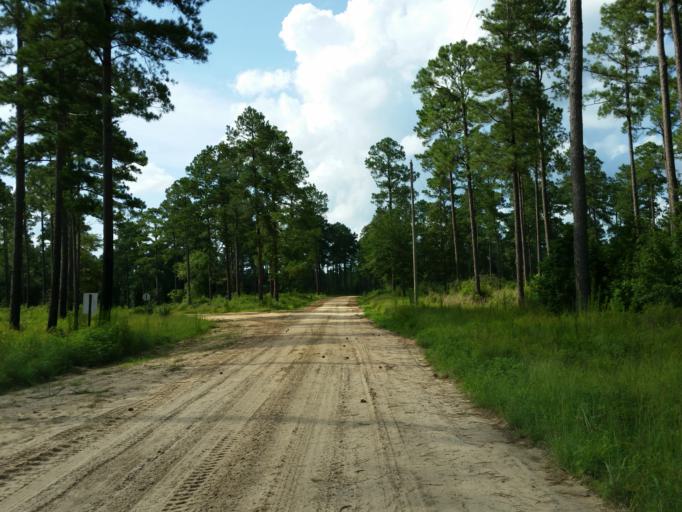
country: US
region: Georgia
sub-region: Lee County
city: Leesburg
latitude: 31.7609
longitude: -84.0183
